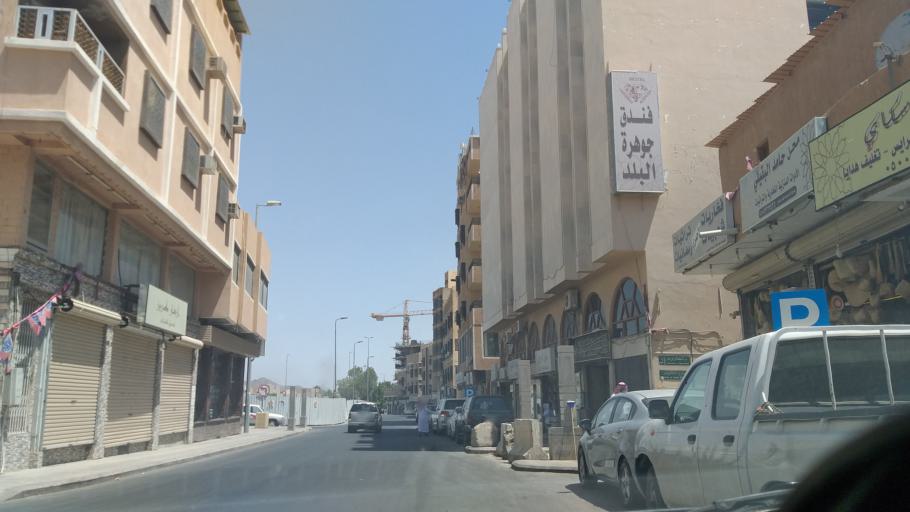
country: SA
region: Makkah
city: Ta'if
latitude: 21.2718
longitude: 40.4074
